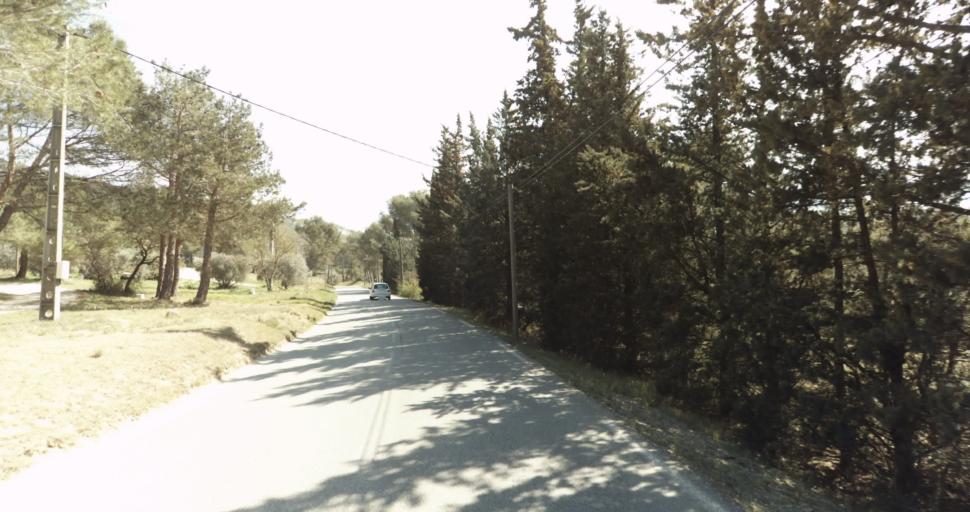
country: FR
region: Provence-Alpes-Cote d'Azur
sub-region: Departement des Bouches-du-Rhone
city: Ventabren
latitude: 43.5276
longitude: 5.2868
